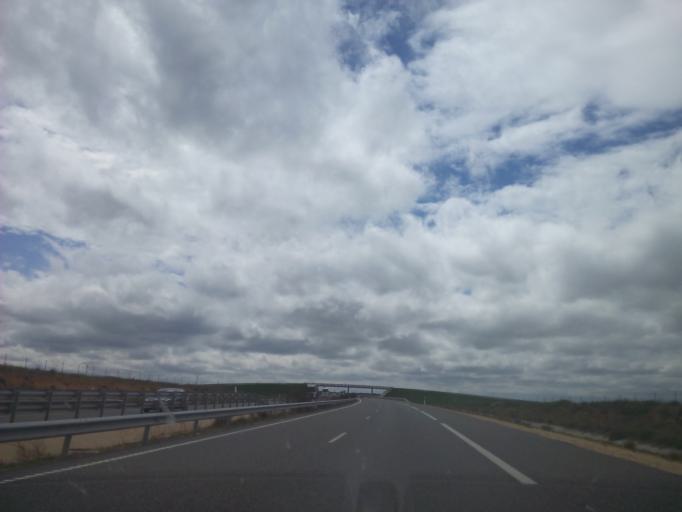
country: ES
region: Castille and Leon
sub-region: Provincia de Salamanca
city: Pelabravo
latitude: 40.9315
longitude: -5.5700
